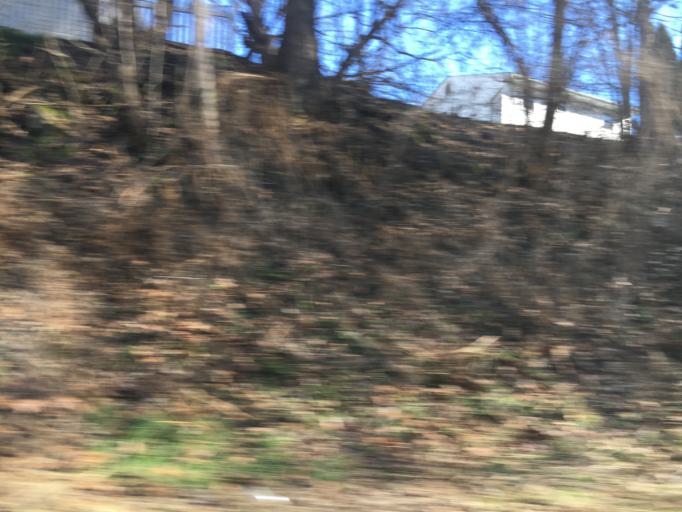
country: US
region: Pennsylvania
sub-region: Lehigh County
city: Allentown
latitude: 40.6336
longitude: -75.5079
